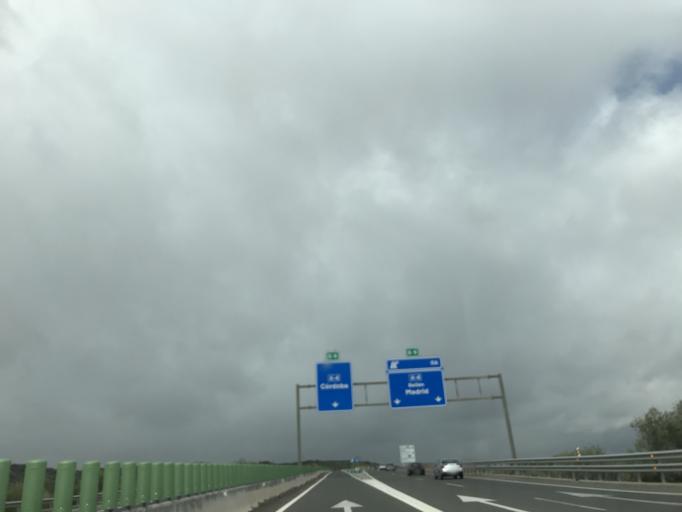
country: ES
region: Andalusia
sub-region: Provincia de Jaen
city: Bailen
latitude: 38.1176
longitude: -3.7569
